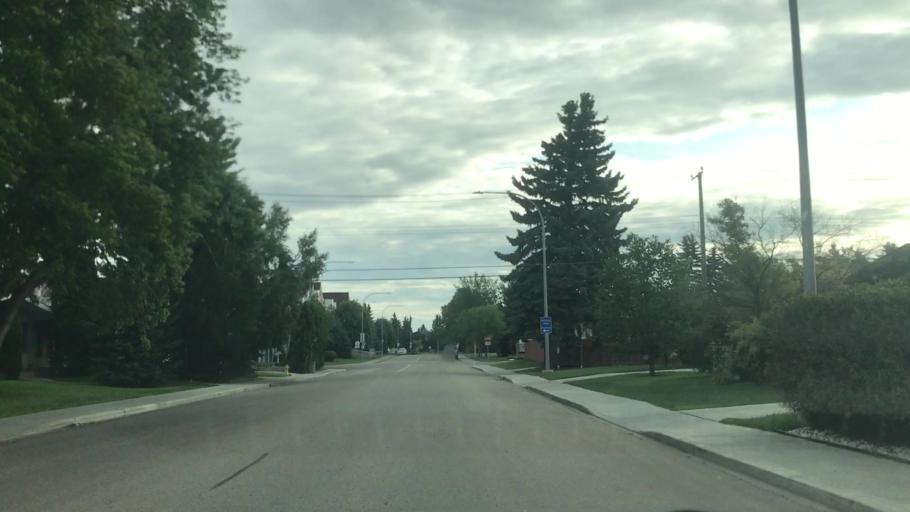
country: CA
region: Alberta
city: Edmonton
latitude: 53.5445
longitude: -113.4286
